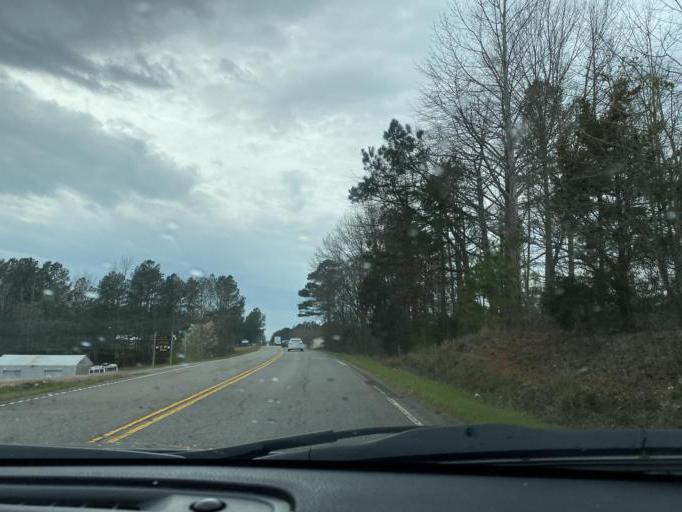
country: US
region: South Carolina
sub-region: Spartanburg County
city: Cowpens
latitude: 35.0158
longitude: -81.7534
